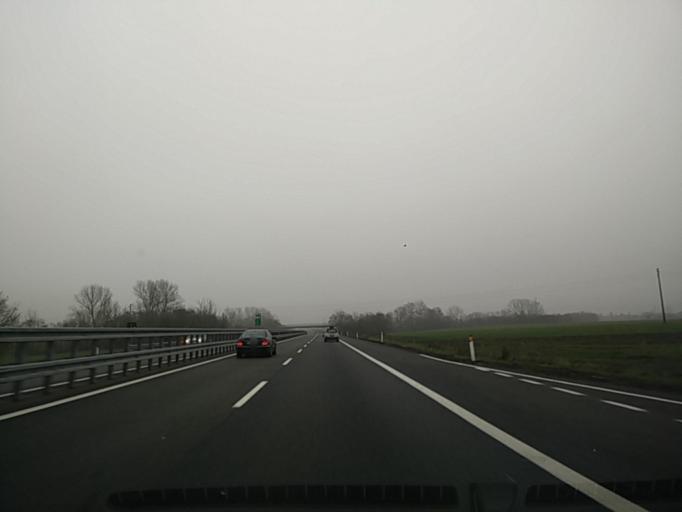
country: IT
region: Piedmont
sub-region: Provincia di Alessandria
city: Solero
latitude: 44.9227
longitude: 8.4848
